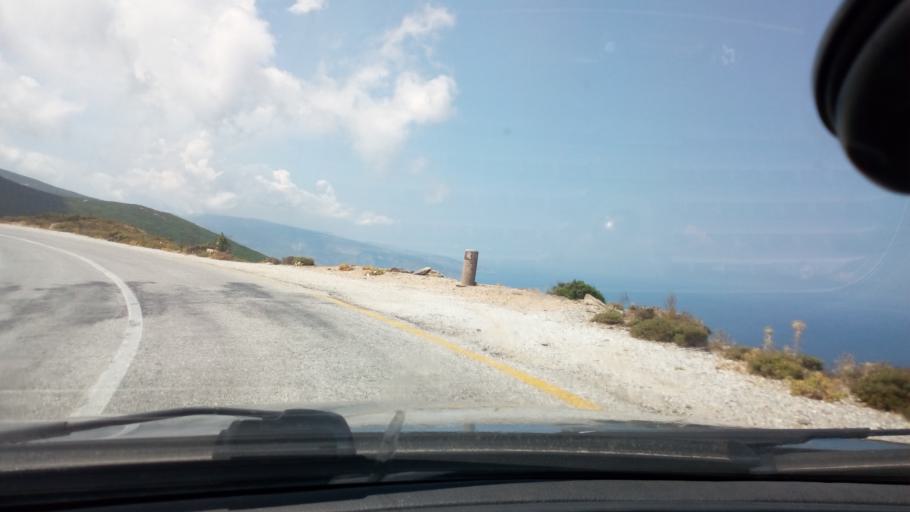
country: GR
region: North Aegean
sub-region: Nomos Samou
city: Agios Kirykos
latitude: 37.6531
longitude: 26.2844
